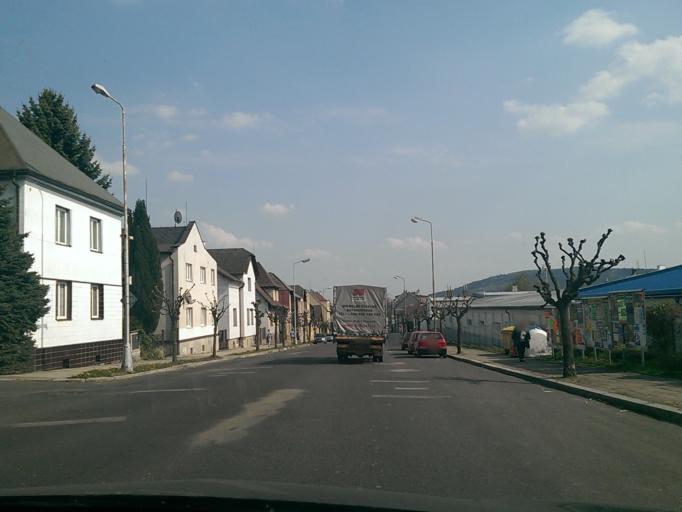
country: CZ
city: Ohrazenice
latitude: 50.5908
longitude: 15.1312
